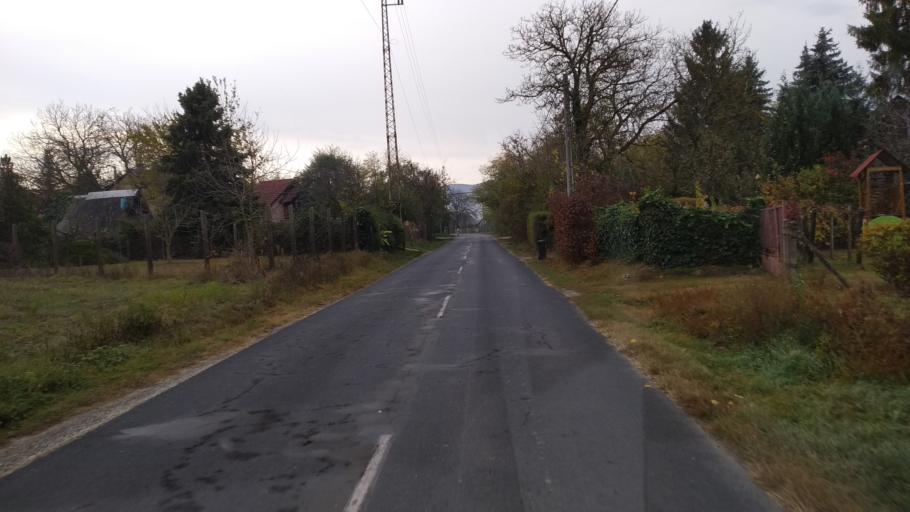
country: HU
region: Pest
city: Tahitotfalu
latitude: 47.7715
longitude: 19.0886
